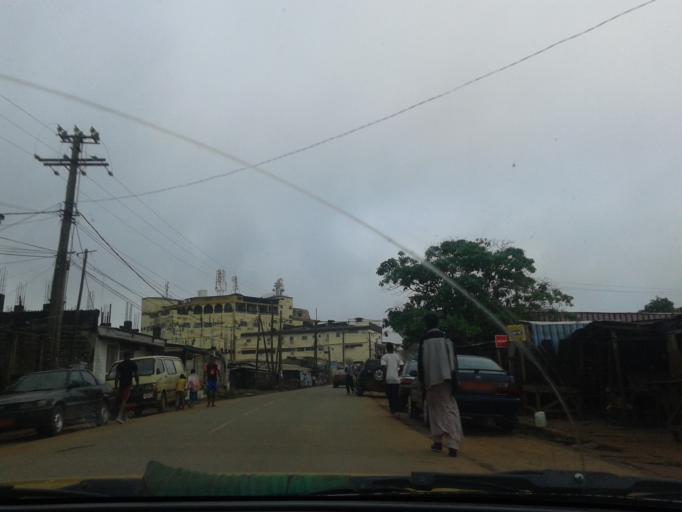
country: CM
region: Centre
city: Yaounde
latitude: 3.8831
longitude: 11.5252
